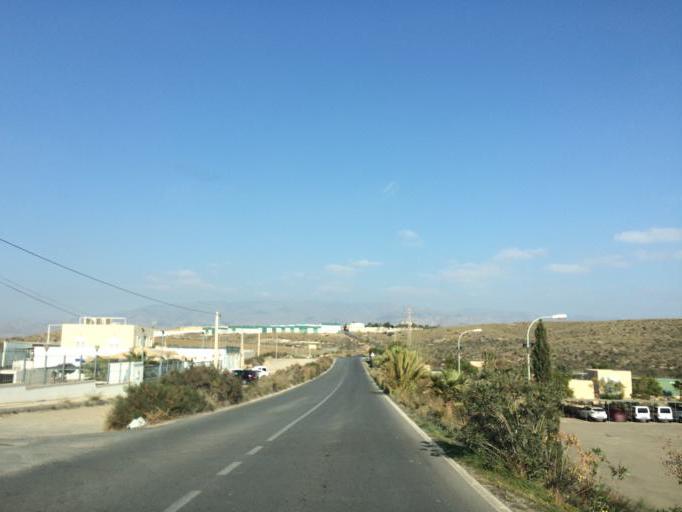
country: ES
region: Andalusia
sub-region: Provincia de Almeria
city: Viator
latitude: 36.8685
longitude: -2.4191
